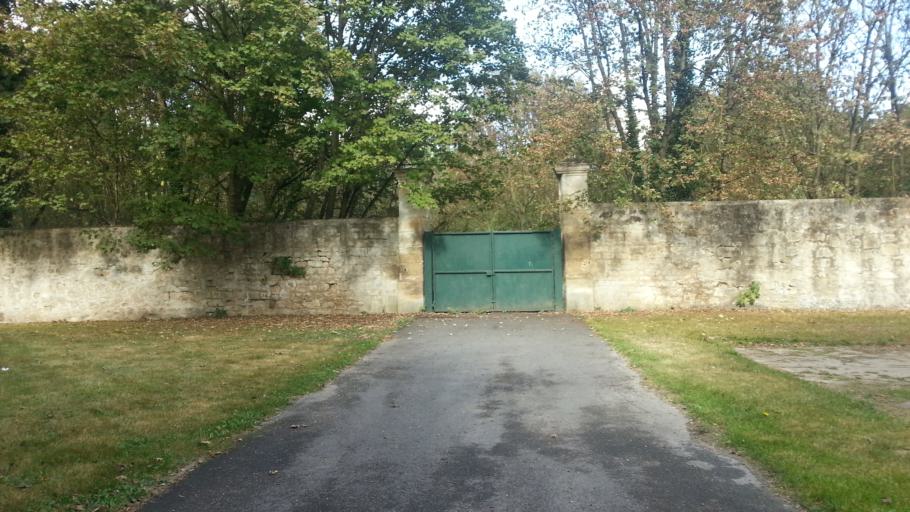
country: FR
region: Picardie
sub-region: Departement de l'Oise
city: Saint-Maximin
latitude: 49.2375
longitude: 2.4572
